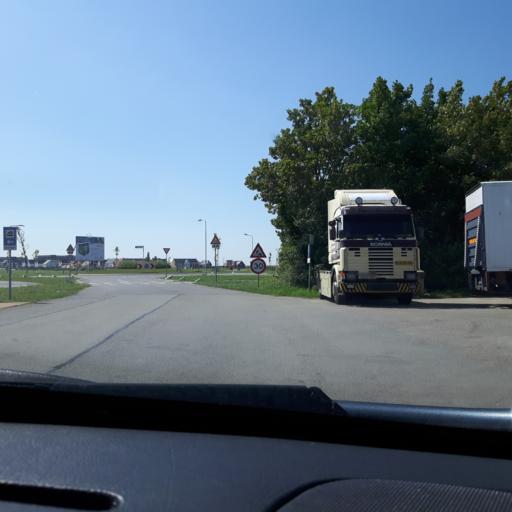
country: NL
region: Zeeland
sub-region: Gemeente Reimerswaal
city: Yerseke
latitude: 51.4439
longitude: 4.0399
